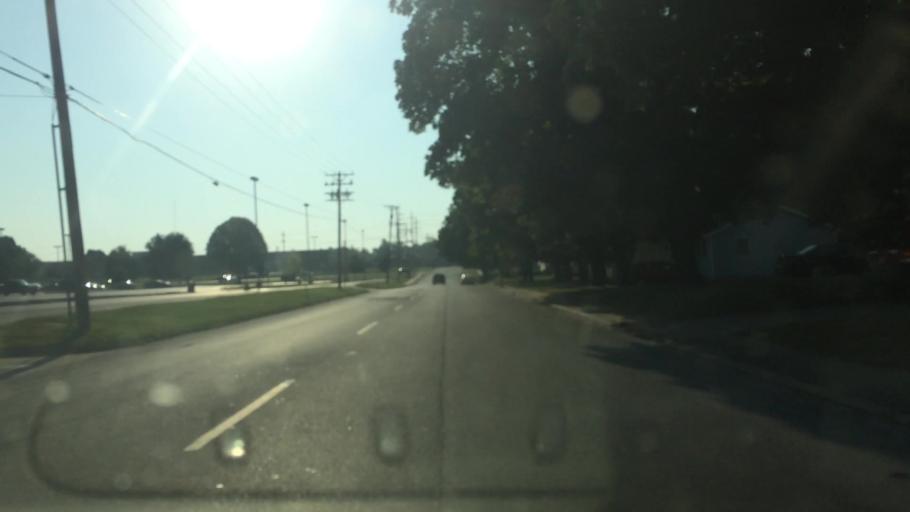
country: US
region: Missouri
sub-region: Greene County
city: Springfield
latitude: 37.2183
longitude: -93.2646
